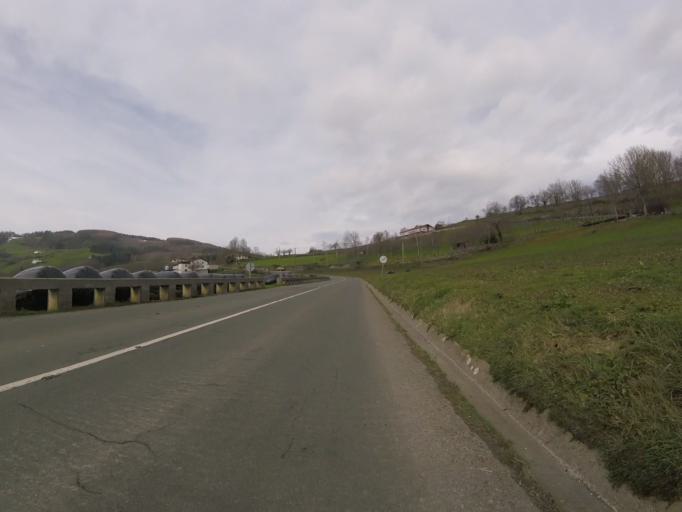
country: ES
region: Basque Country
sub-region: Provincia de Guipuzcoa
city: Errezil
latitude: 43.1434
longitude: -2.1725
